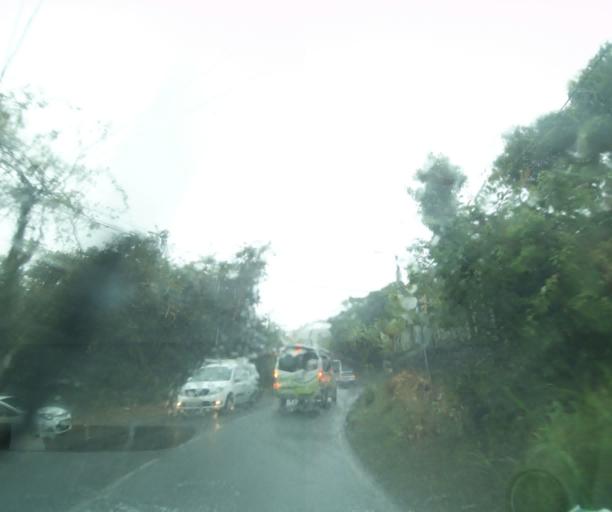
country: RE
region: Reunion
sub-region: Reunion
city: Saint-Paul
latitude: -20.9961
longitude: 55.3286
